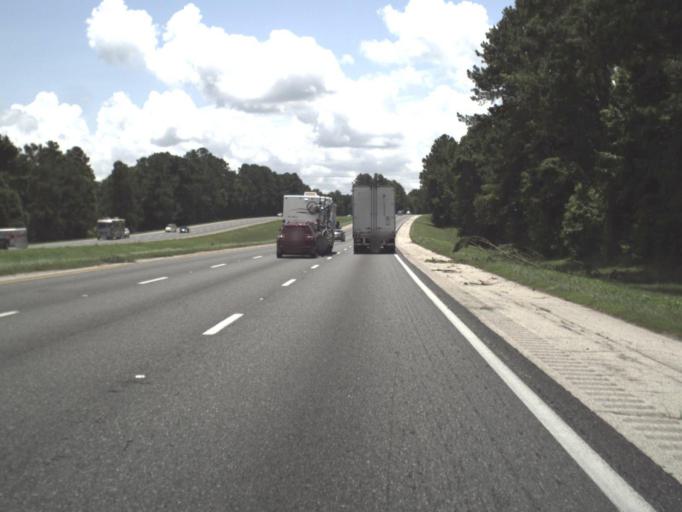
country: US
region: Florida
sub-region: Alachua County
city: Alachua
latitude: 29.7440
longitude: -82.4832
